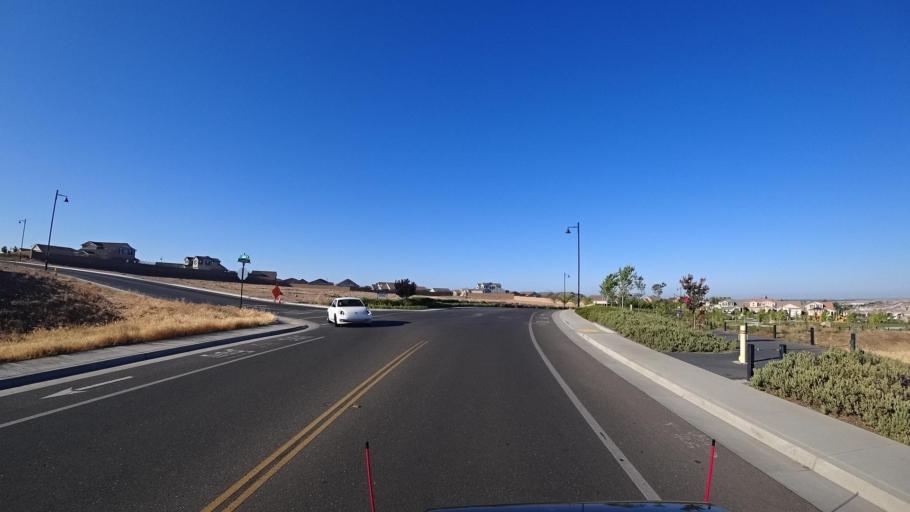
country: US
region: California
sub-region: Placer County
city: Rocklin
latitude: 38.8340
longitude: -121.2693
